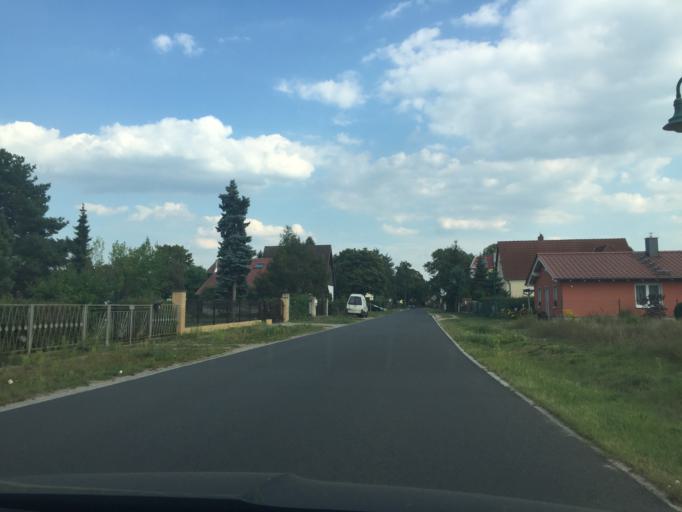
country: DE
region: Brandenburg
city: Erkner
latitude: 52.3850
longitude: 13.7642
